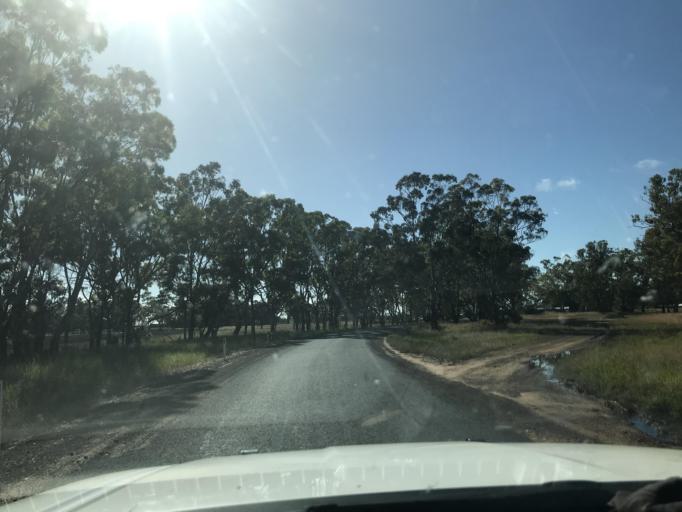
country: AU
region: Victoria
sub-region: Horsham
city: Horsham
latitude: -37.0312
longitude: 141.7261
